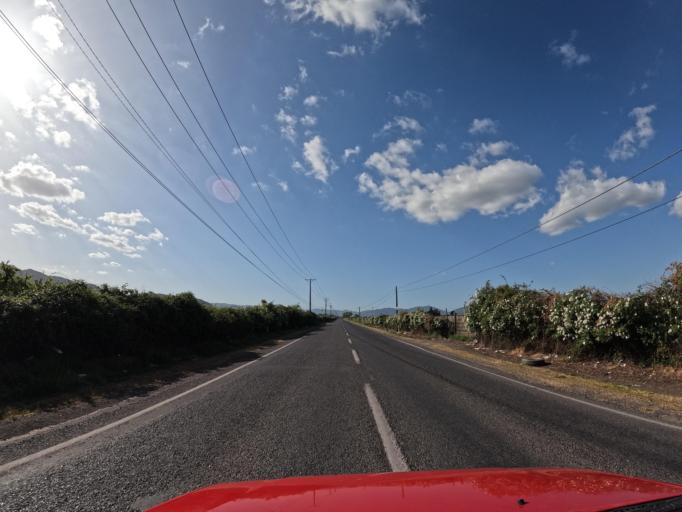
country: CL
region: Maule
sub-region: Provincia de Curico
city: Rauco
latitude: -34.9262
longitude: -71.2768
